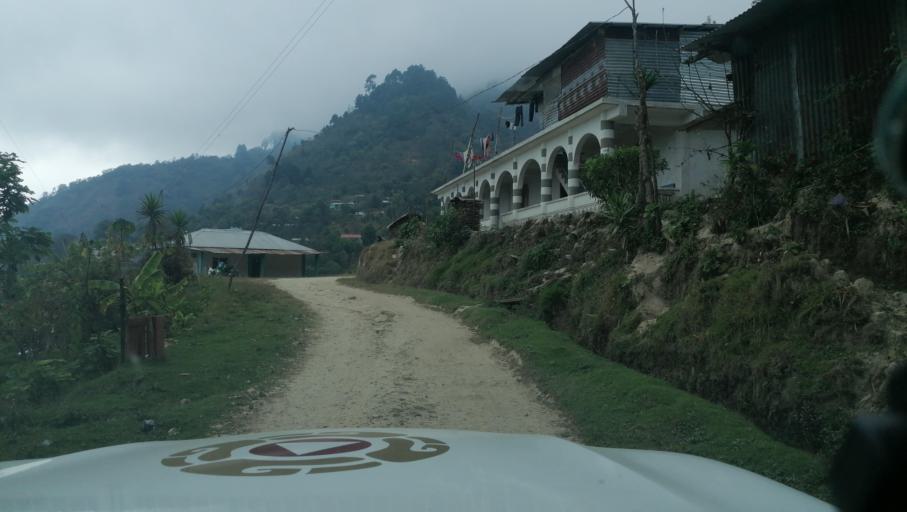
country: GT
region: San Marcos
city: Tacana
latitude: 15.2057
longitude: -92.1692
